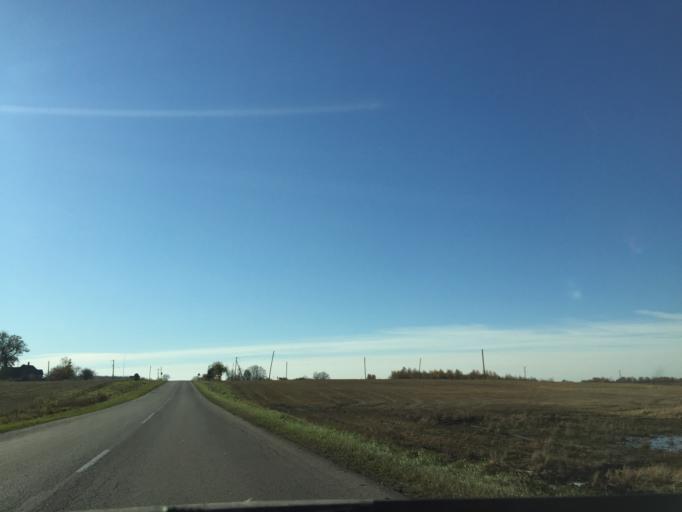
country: LV
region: Skriveri
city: Skriveri
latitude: 56.7056
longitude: 25.1534
